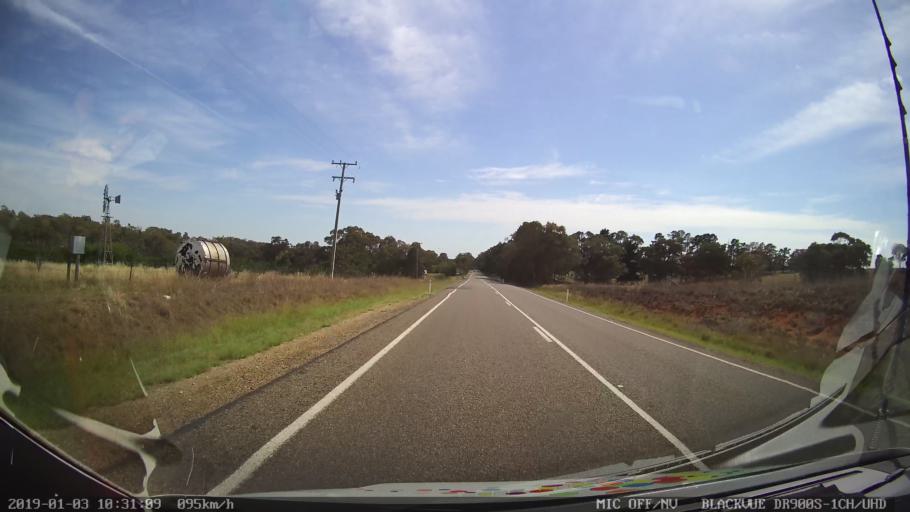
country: AU
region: New South Wales
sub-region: Young
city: Young
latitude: -34.3535
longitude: 148.2744
